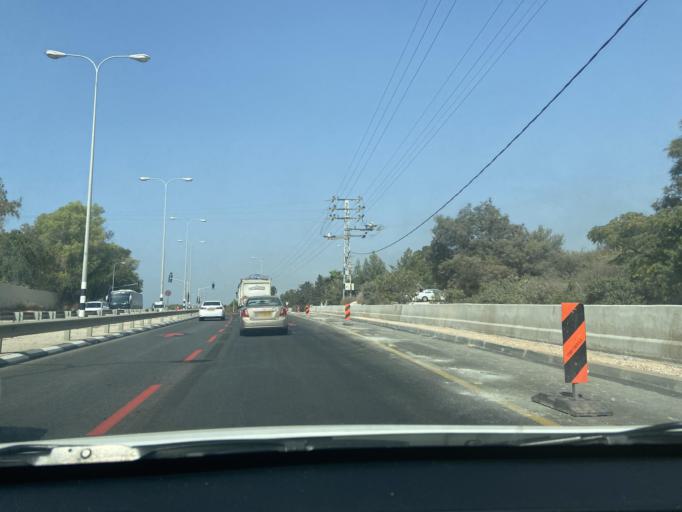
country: IL
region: Northern District
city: El Mazra`a
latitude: 32.9605
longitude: 35.0938
